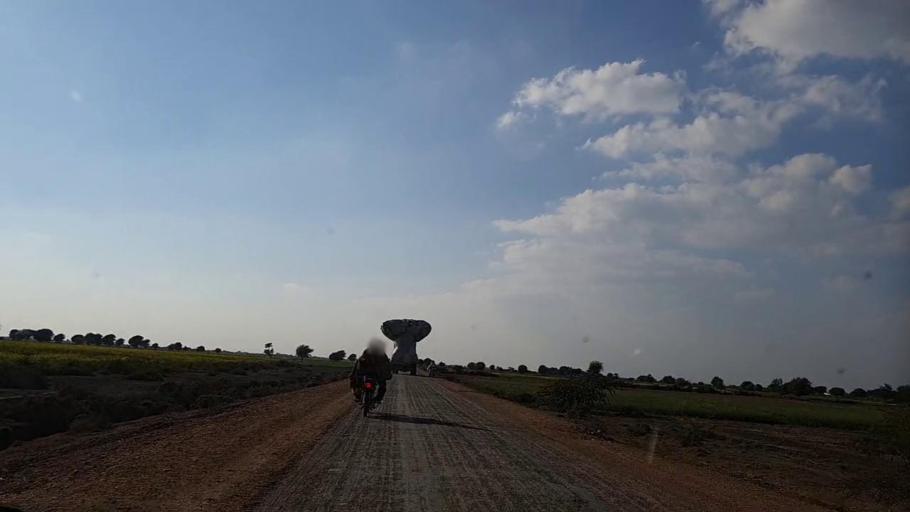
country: PK
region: Sindh
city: Pithoro
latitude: 25.6514
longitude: 69.2622
